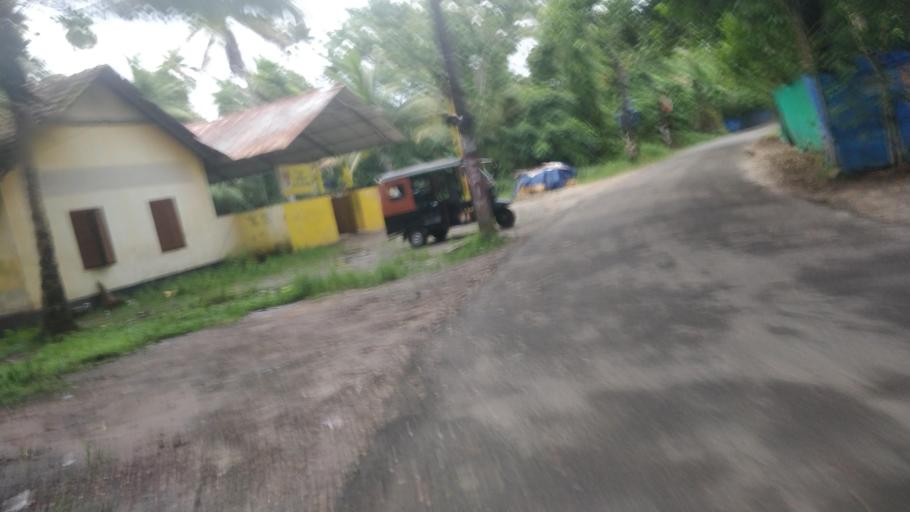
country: IN
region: Kerala
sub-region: Alappuzha
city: Vayalar
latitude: 9.7050
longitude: 76.3484
